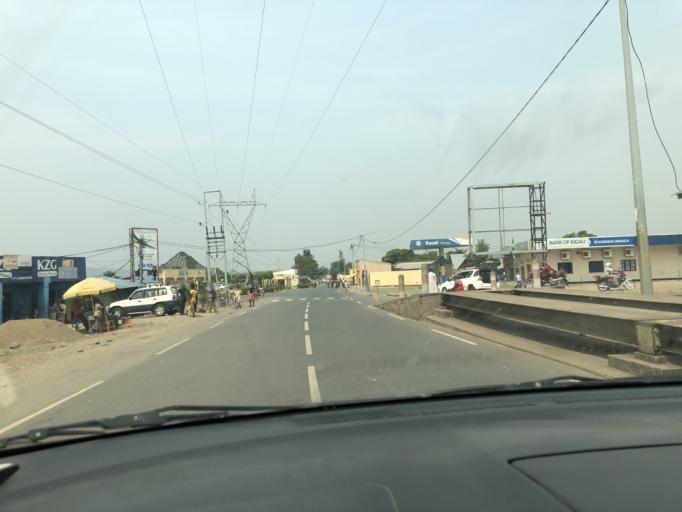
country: BI
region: Cibitoke
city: Cibitoke
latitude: -2.6991
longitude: 29.0055
